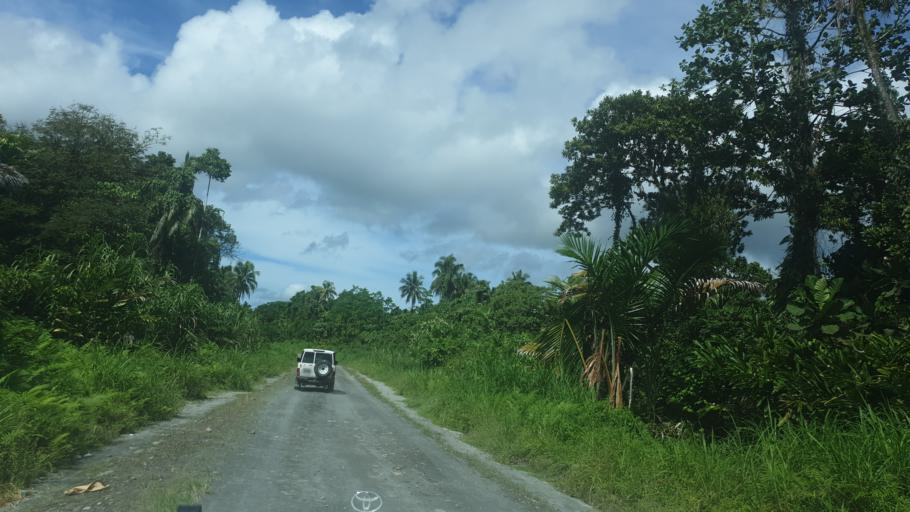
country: PG
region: Bougainville
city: Panguna
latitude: -6.5562
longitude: 155.3536
